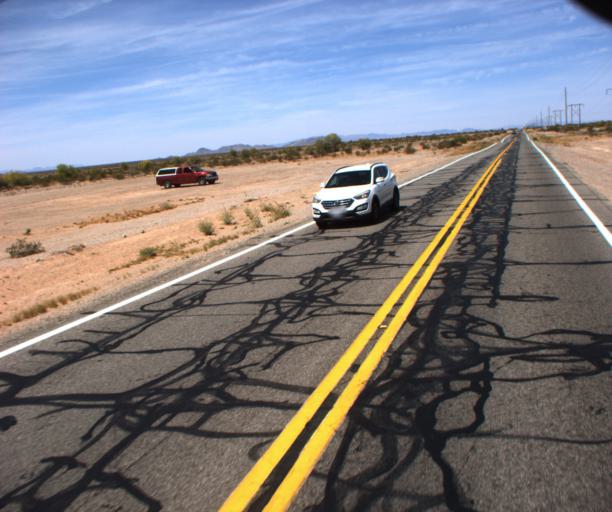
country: US
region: Arizona
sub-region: La Paz County
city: Quartzsite
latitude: 33.8184
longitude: -114.2170
